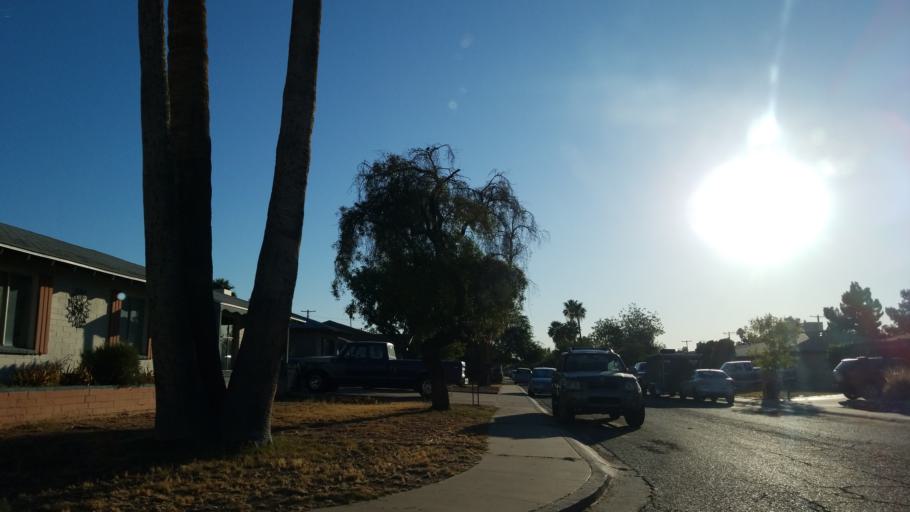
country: US
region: Arizona
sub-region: Maricopa County
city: Glendale
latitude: 33.5691
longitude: -112.0946
